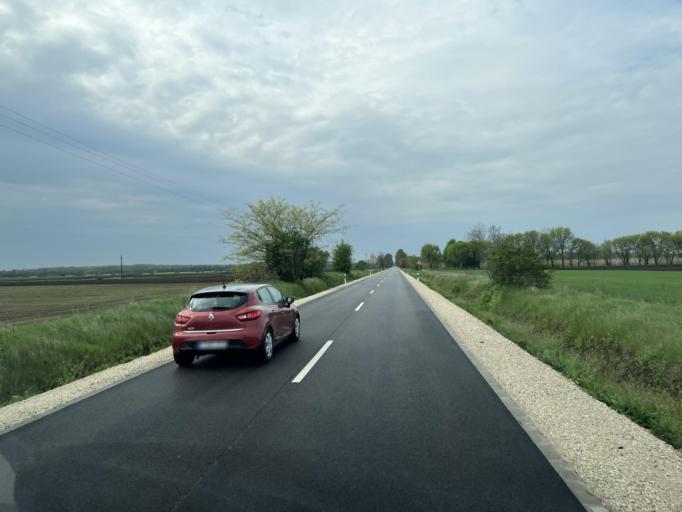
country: HU
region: Pest
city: Nyaregyhaza
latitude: 47.2419
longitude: 19.5204
